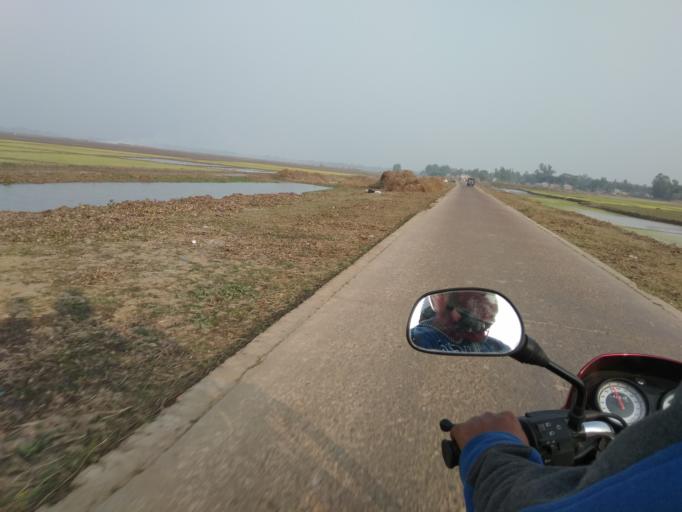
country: BD
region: Rajshahi
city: Ishurdi
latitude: 24.4821
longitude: 89.2273
